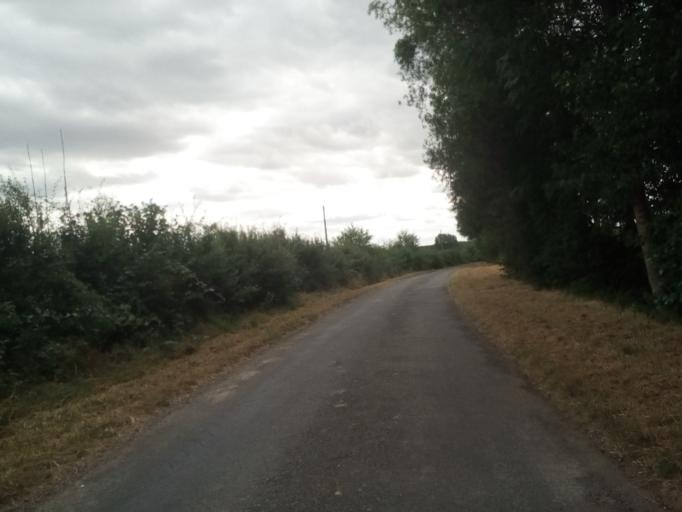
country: FR
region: Lower Normandy
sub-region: Departement du Calvados
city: Argences
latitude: 49.1545
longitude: -0.1581
